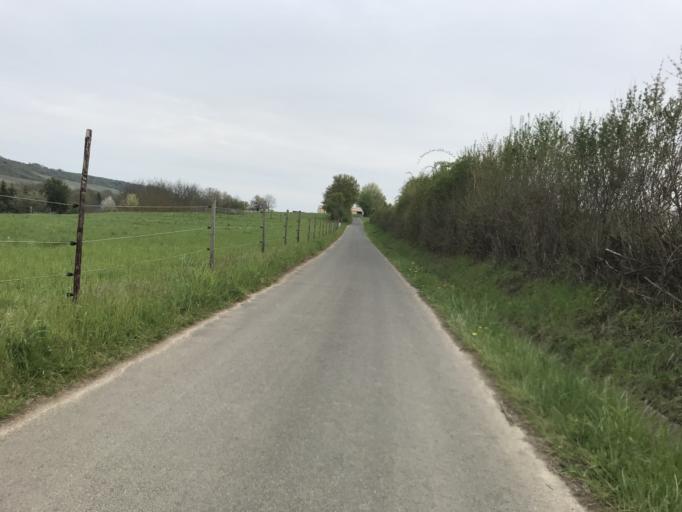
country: DE
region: Rheinland-Pfalz
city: Gau-Algesheim
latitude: 49.9429
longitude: 8.0220
